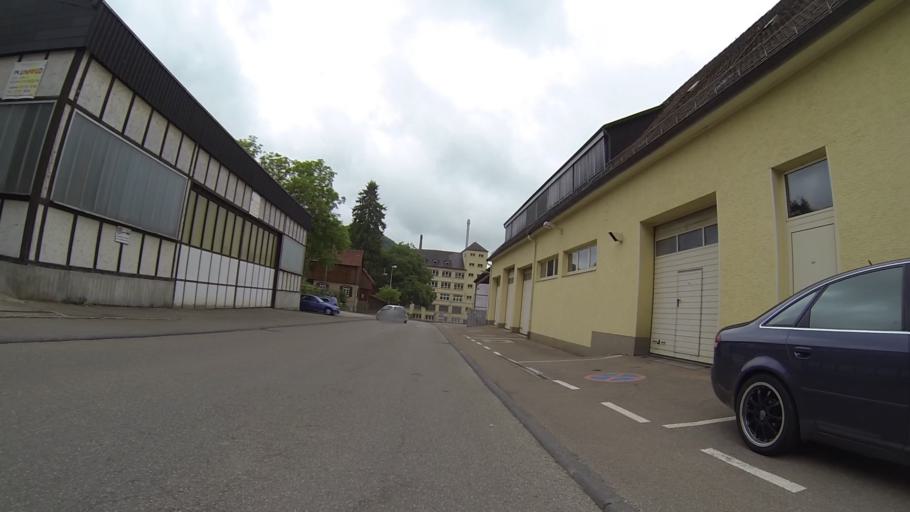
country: DE
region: Baden-Wuerttemberg
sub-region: Regierungsbezirk Stuttgart
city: Heubach
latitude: 48.7868
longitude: 9.9386
